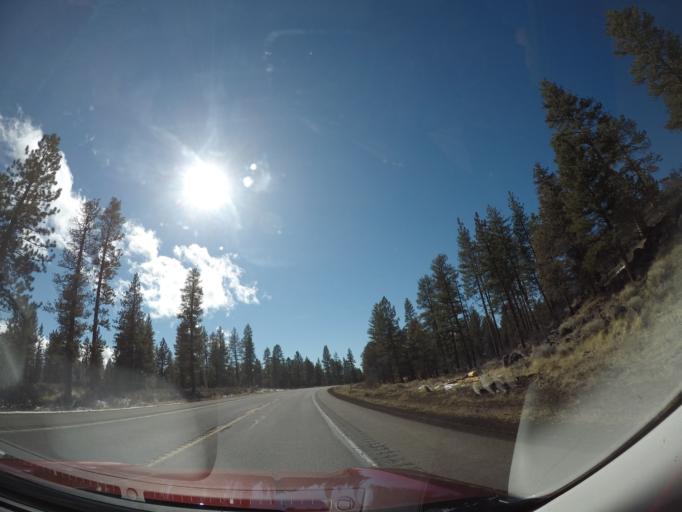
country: US
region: California
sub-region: Siskiyou County
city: Weed
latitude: 41.6736
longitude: -122.0755
